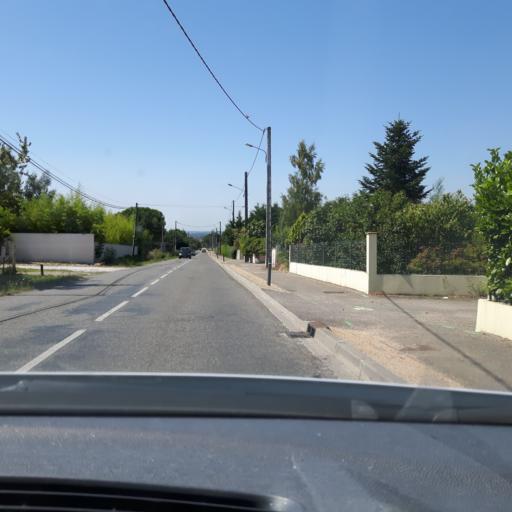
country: FR
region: Midi-Pyrenees
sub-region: Departement de la Haute-Garonne
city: Bouloc
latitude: 43.7767
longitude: 1.3944
